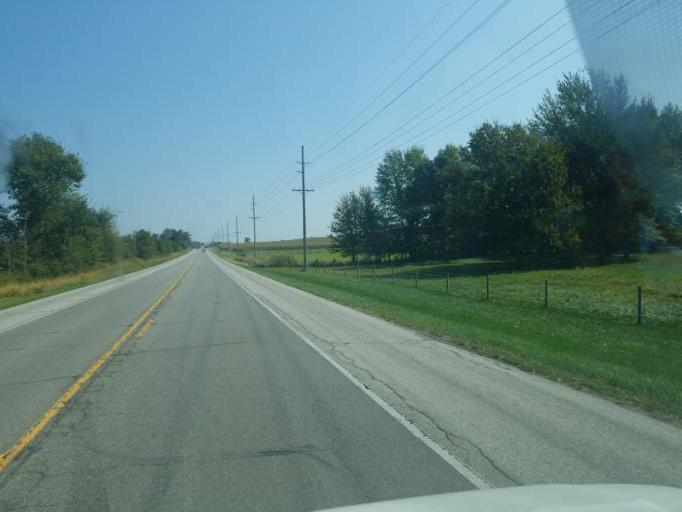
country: US
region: Indiana
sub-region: LaGrange County
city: Lagrange
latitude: 41.6417
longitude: -85.3830
